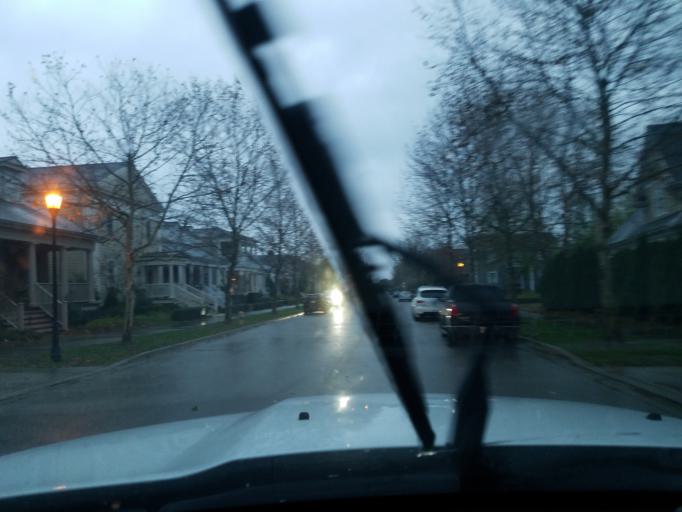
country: US
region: Kentucky
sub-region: Jefferson County
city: Worthington
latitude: 38.3235
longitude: -85.5642
